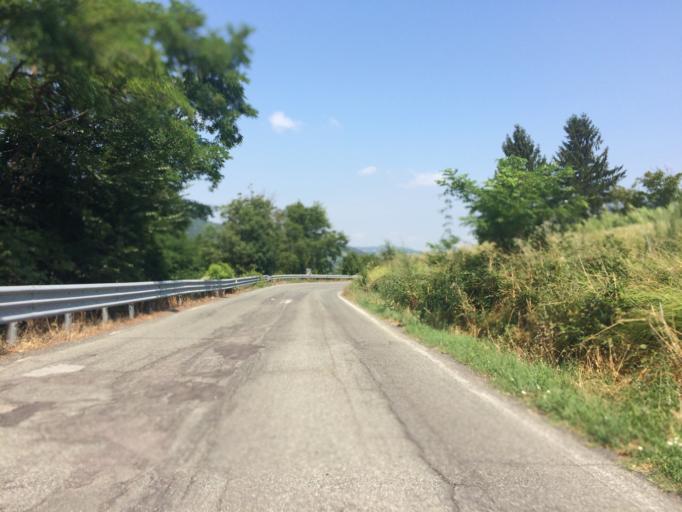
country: IT
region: Piedmont
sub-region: Provincia di Alessandria
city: Castelletto d'Erro
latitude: 44.6177
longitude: 8.4145
